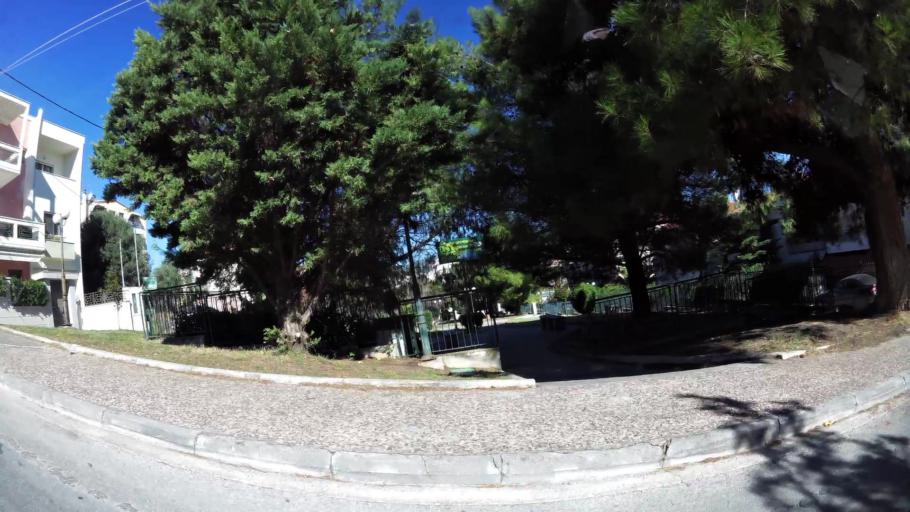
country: GR
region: Attica
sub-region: Nomarchia Anatolikis Attikis
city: Leondarion
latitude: 38.0012
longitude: 23.8573
